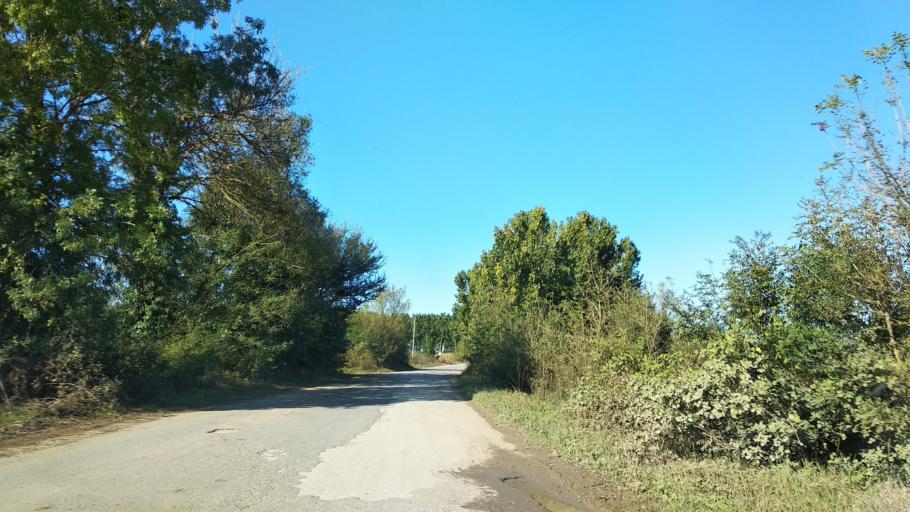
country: TR
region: Sakarya
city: Ortakoy
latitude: 41.0279
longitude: 30.6068
